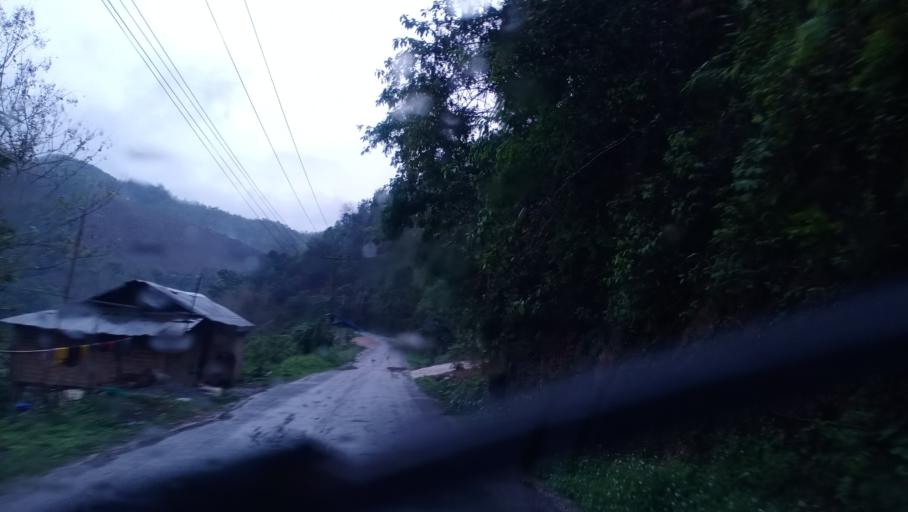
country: LA
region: Phongsali
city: Khoa
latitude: 21.0660
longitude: 102.4865
